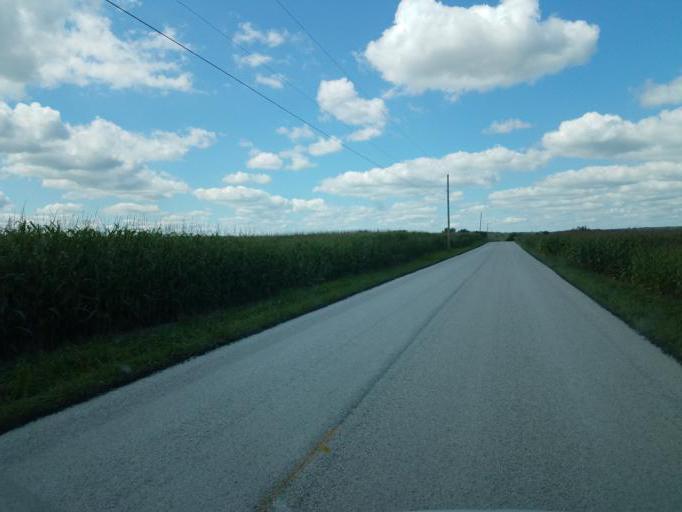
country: US
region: Ohio
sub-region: Wayne County
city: West Salem
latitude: 40.9745
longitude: -82.2366
